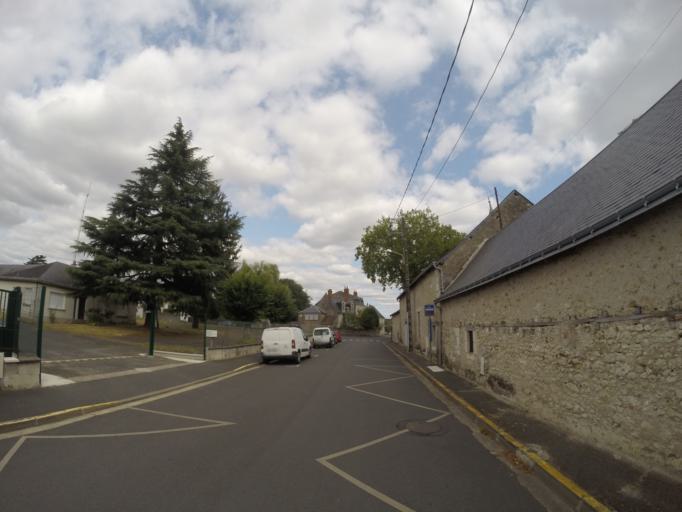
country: FR
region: Centre
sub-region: Departement d'Indre-et-Loire
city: Tours
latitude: 47.4121
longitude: 0.7080
